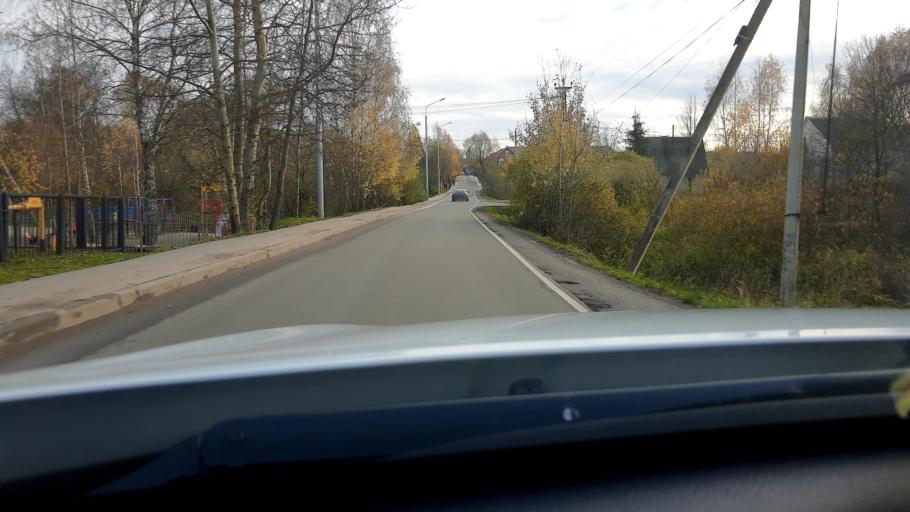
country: RU
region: Moskovskaya
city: Kokoshkino
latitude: 55.5293
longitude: 37.1545
